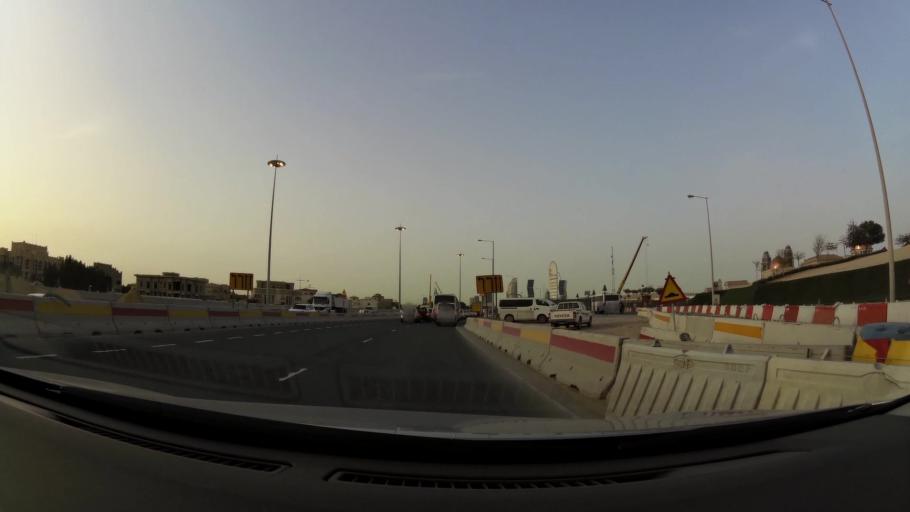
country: QA
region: Baladiyat ad Dawhah
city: Doha
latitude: 25.3599
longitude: 51.5209
